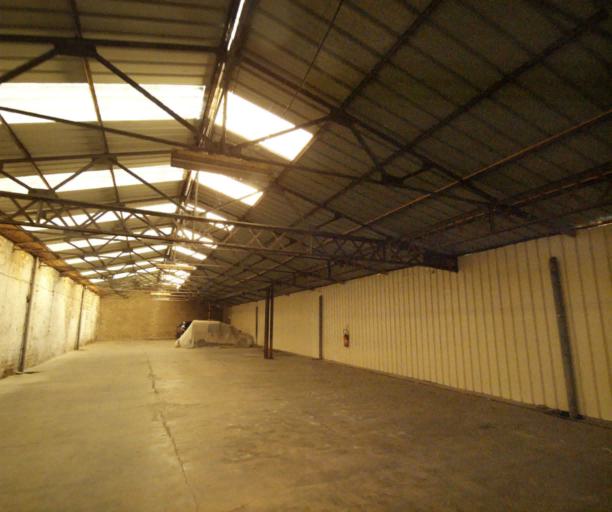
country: FR
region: Champagne-Ardenne
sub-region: Departement des Ardennes
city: Charleville-Mezieres
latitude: 49.7665
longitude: 4.7223
